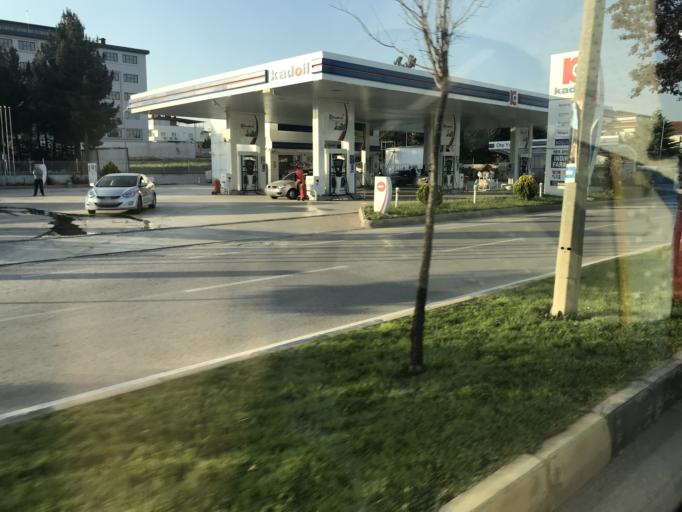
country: TR
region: Gaziantep
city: Sahinbey
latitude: 37.0551
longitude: 37.3253
